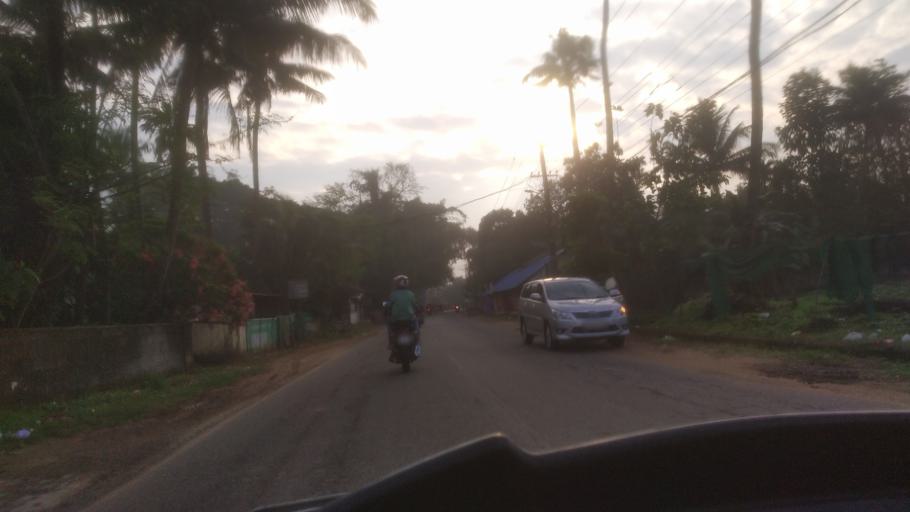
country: IN
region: Kerala
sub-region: Ernakulam
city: Perumpavur
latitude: 10.1201
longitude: 76.4371
